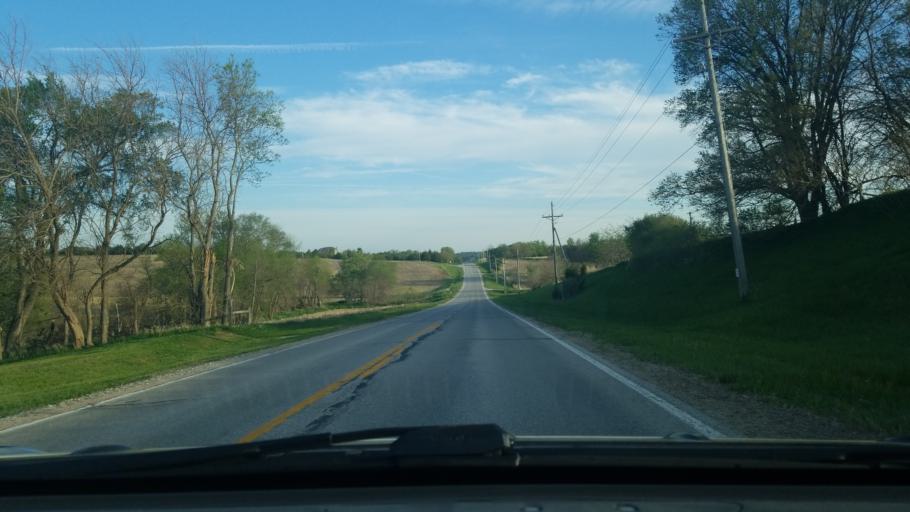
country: US
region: Nebraska
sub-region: Sarpy County
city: Offutt Air Force Base
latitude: 41.0823
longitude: -95.9665
